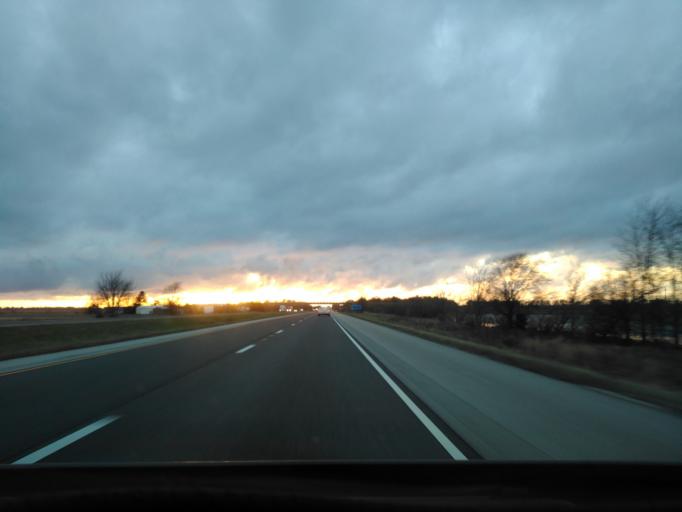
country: US
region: Illinois
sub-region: Fayette County
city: Saint Elmo
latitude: 39.0222
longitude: -88.8200
